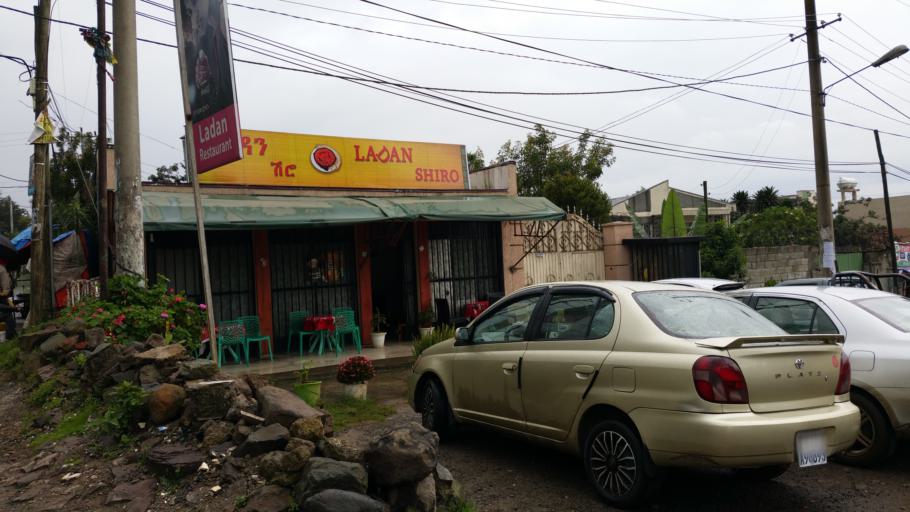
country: ET
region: Adis Abeba
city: Addis Ababa
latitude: 9.0247
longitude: 38.7863
